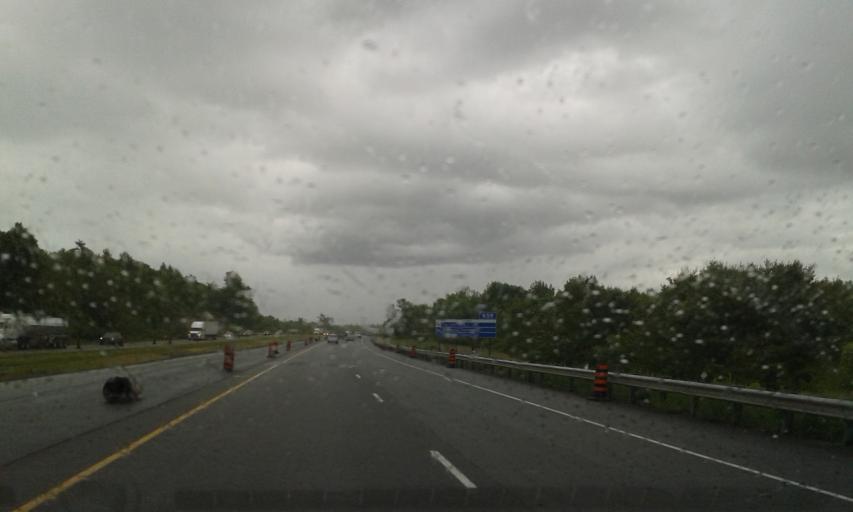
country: US
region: New York
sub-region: Jefferson County
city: Alexandria Bay
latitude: 44.3762
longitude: -76.0421
